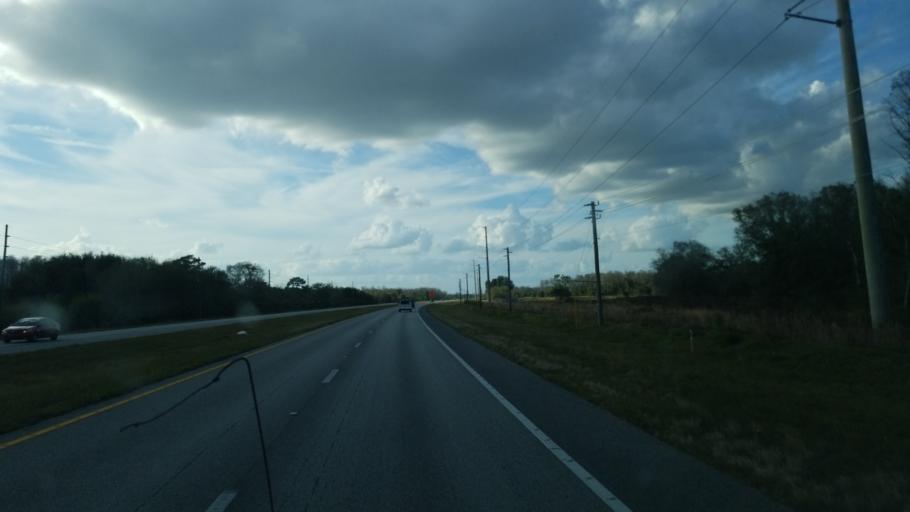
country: US
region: Florida
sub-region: Osceola County
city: Saint Cloud
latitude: 28.1513
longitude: -81.1032
